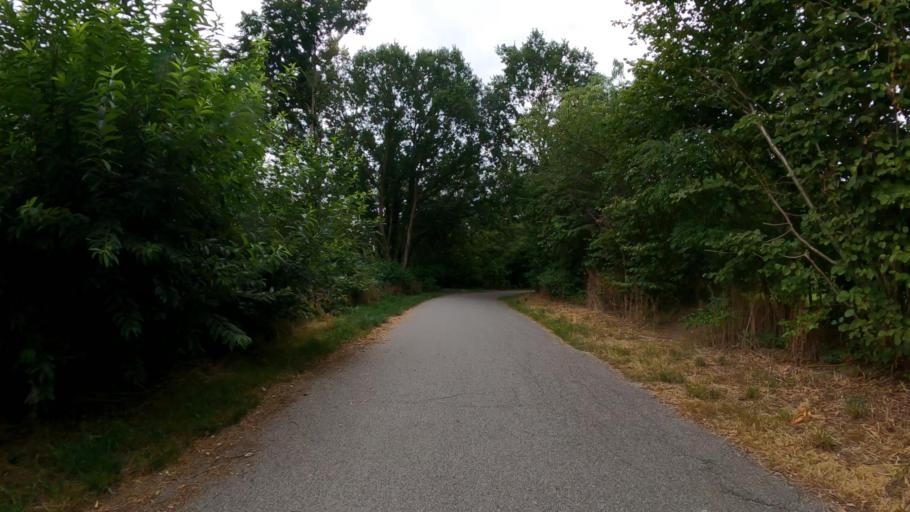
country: DE
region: Schleswig-Holstein
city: Neumunster
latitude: 54.0599
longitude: 10.0194
